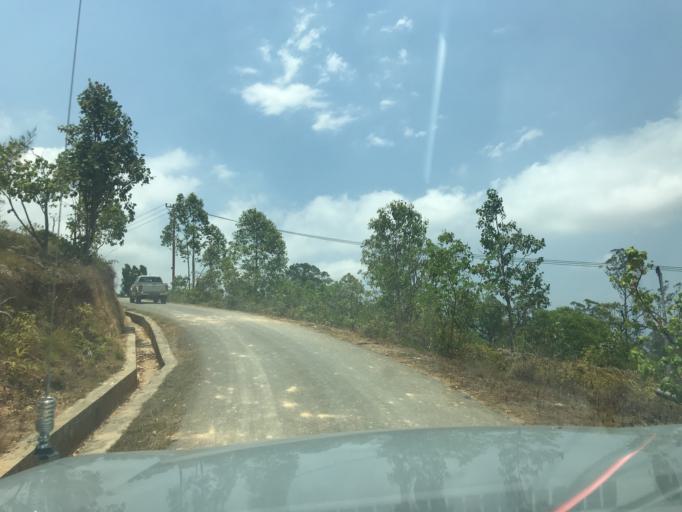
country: TL
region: Dili
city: Dili
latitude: -8.6072
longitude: 125.5882
